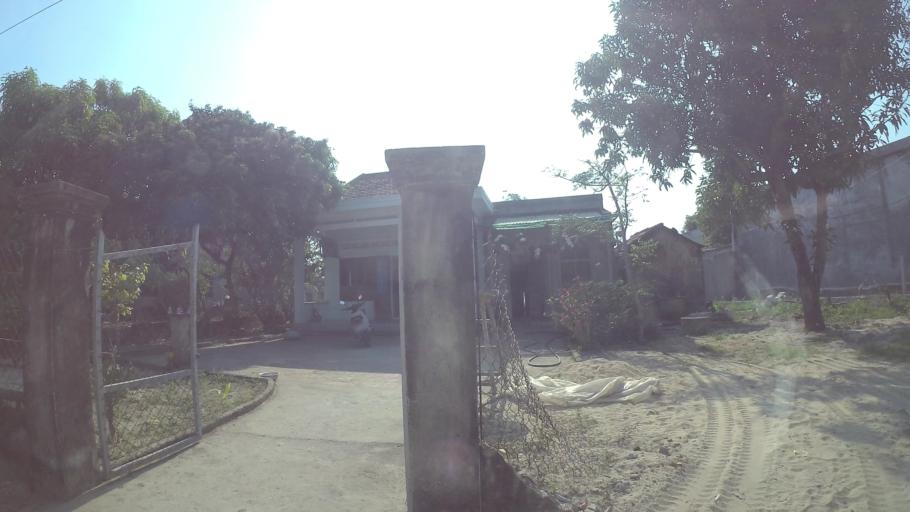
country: VN
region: Da Nang
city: Ngu Hanh Son
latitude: 15.9563
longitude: 108.2649
